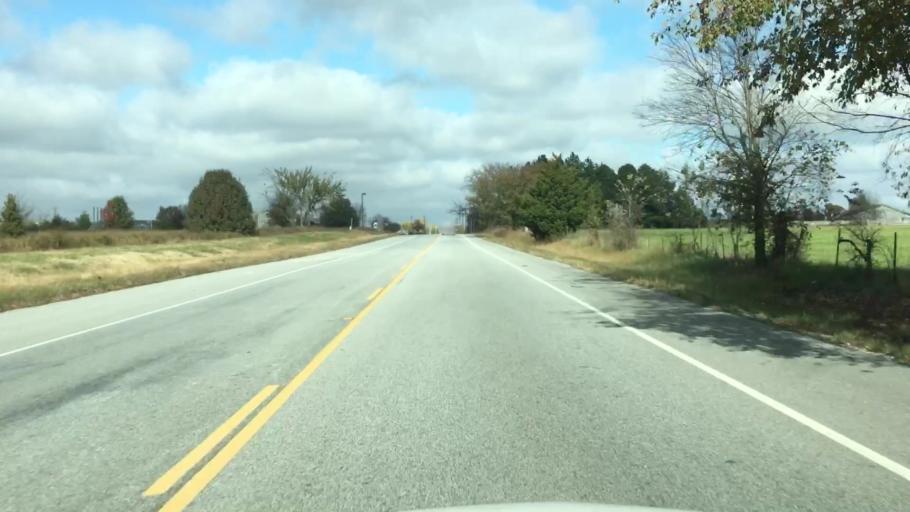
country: US
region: Arkansas
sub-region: Benton County
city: Centerton
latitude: 36.3061
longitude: -94.3038
